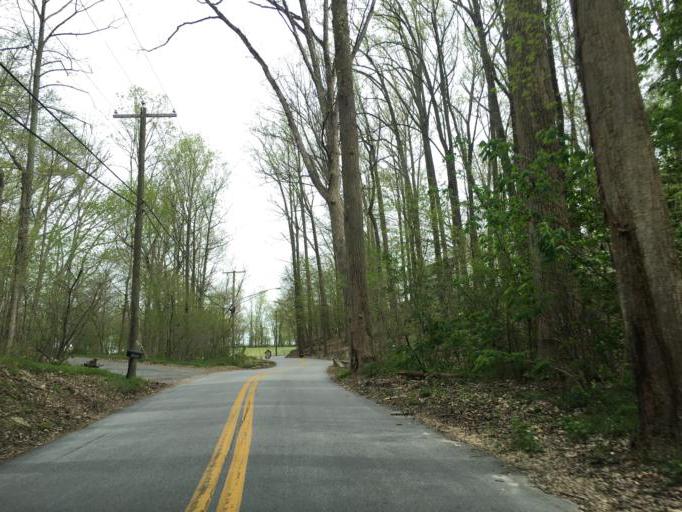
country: US
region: Maryland
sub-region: Baltimore County
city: Hunt Valley
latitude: 39.5523
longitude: -76.6243
